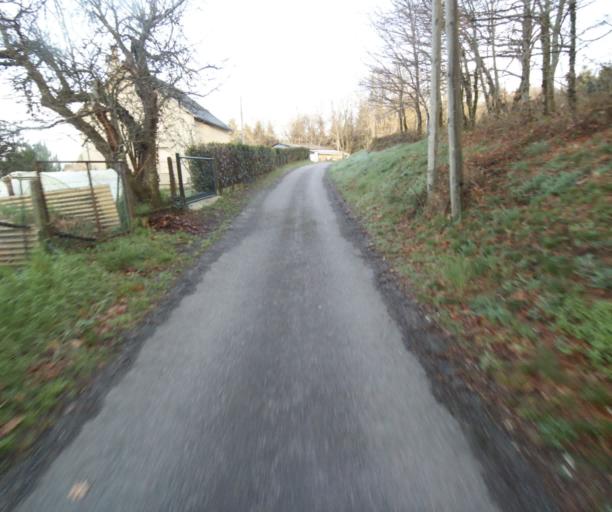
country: FR
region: Limousin
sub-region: Departement de la Correze
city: Correze
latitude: 45.3087
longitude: 1.8492
